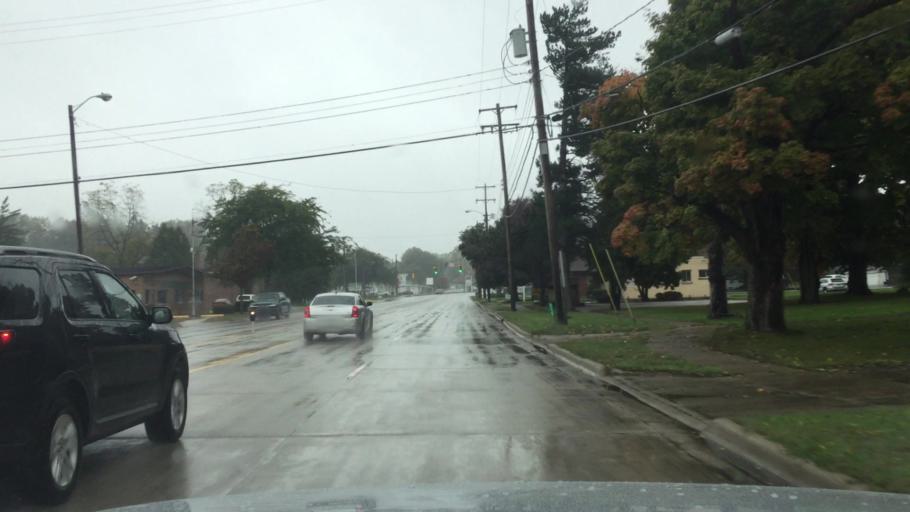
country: US
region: Michigan
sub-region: Saginaw County
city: Bridgeport
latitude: 43.3566
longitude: -83.8772
